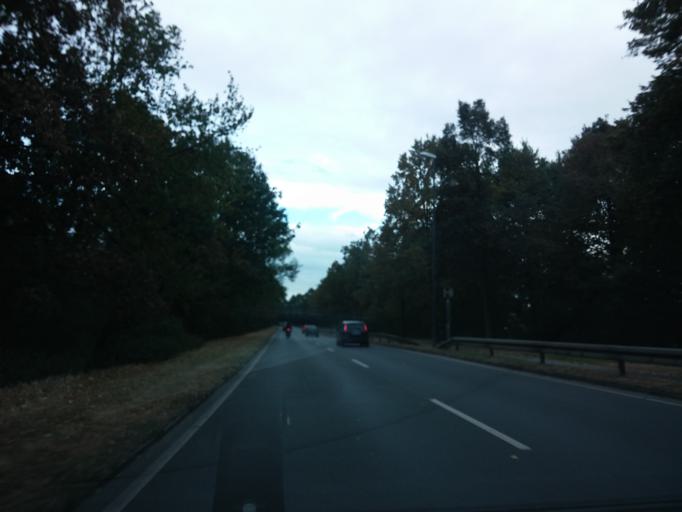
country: DE
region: North Rhine-Westphalia
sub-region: Regierungsbezirk Munster
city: Gladbeck
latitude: 51.5578
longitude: 7.0595
